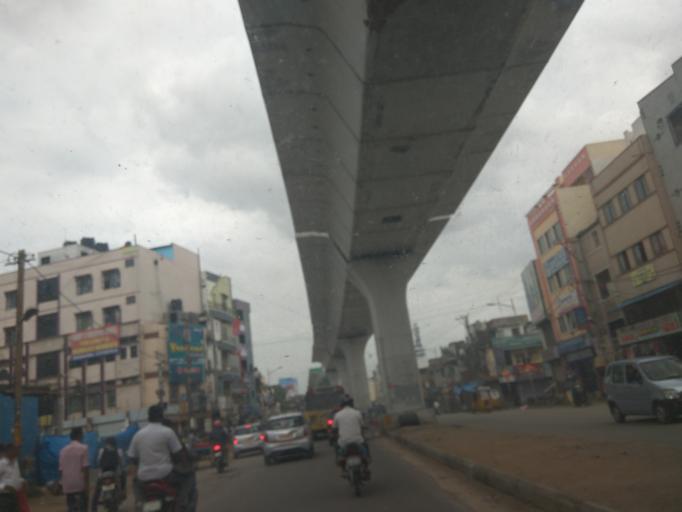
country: IN
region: Telangana
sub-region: Hyderabad
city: Hyderabad
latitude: 17.4027
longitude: 78.4952
